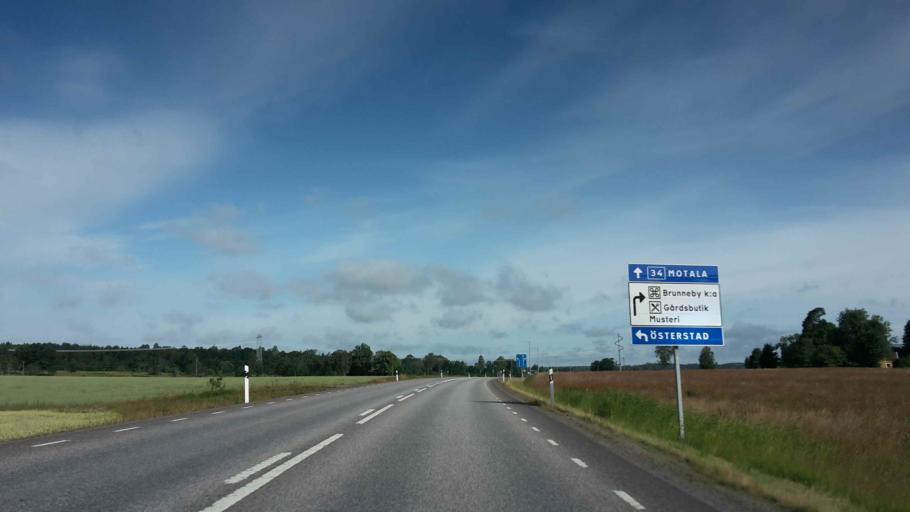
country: SE
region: OEstergoetland
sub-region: Motala Kommun
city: Borensberg
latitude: 58.5378
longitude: 15.3269
